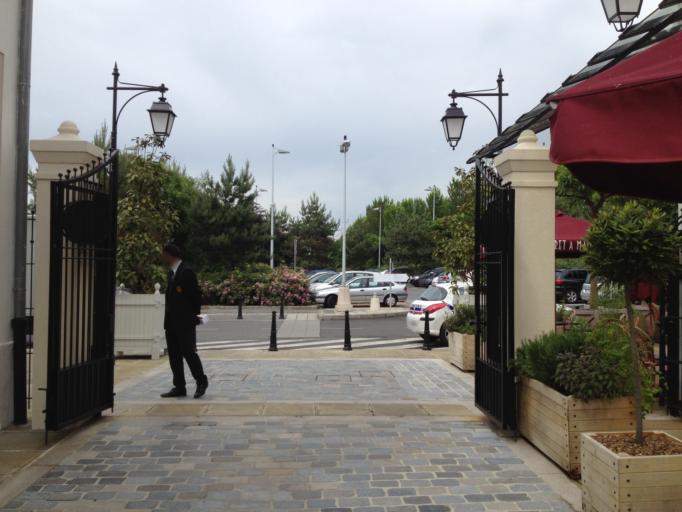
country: FR
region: Ile-de-France
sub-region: Departement de Seine-et-Marne
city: Serris
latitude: 48.8527
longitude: 2.7848
